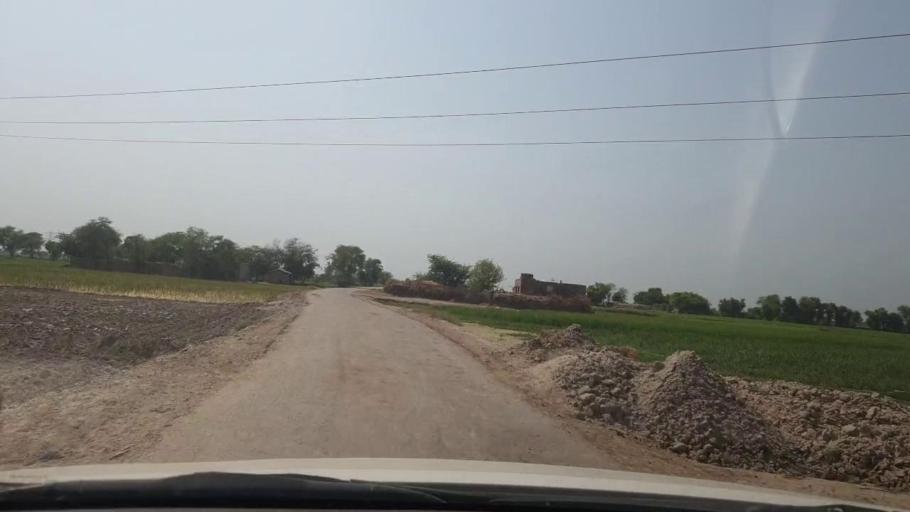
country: PK
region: Sindh
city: Shikarpur
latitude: 28.0035
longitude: 68.7181
